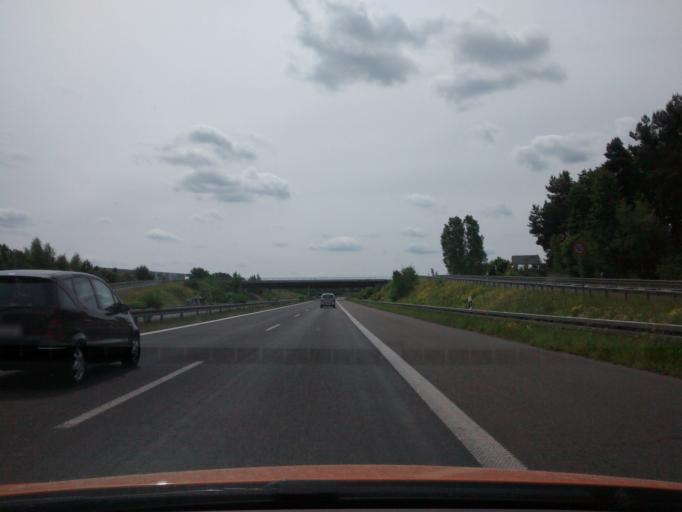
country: DE
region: Brandenburg
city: Grossbeeren
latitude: 52.3310
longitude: 13.2844
